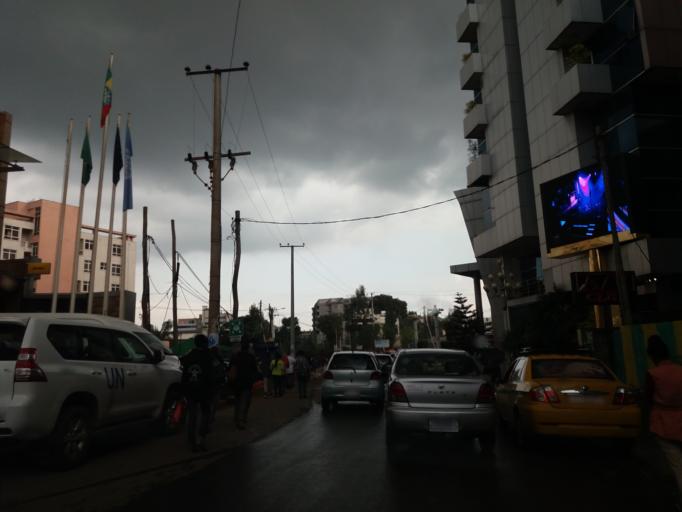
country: ET
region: Adis Abeba
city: Addis Ababa
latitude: 8.9943
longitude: 38.7850
